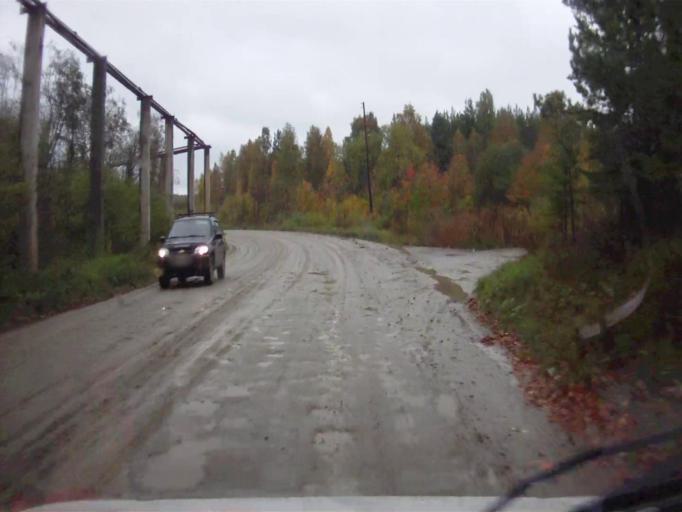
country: RU
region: Chelyabinsk
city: Kyshtym
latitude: 55.7307
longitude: 60.5197
